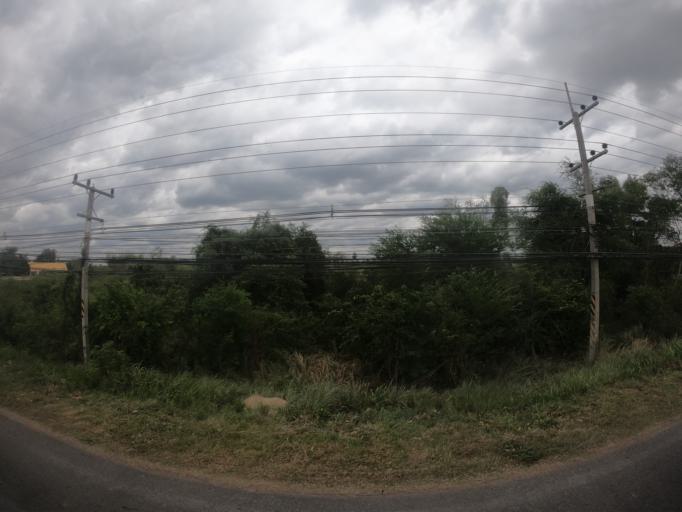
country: TH
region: Nakhon Ratchasima
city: Nakhon Ratchasima
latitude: 14.8992
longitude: 102.1606
